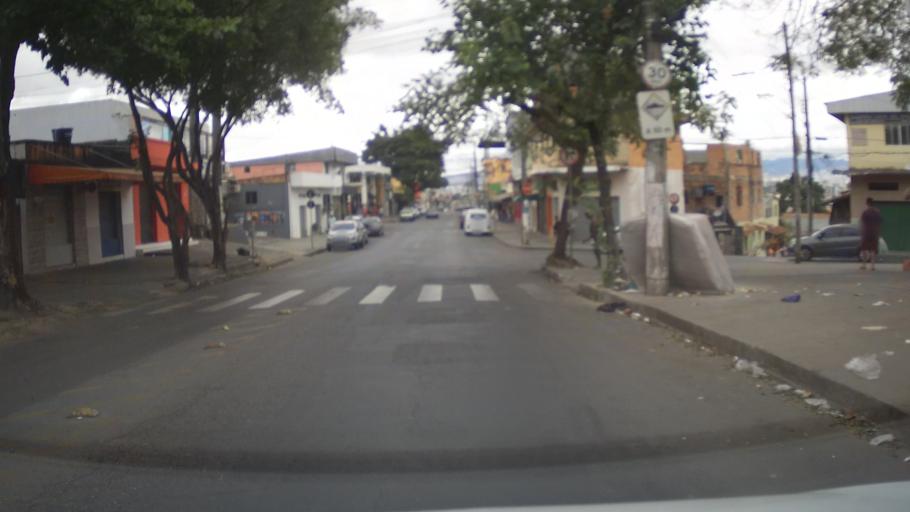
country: BR
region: Minas Gerais
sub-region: Belo Horizonte
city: Belo Horizonte
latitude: -19.8409
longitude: -43.9499
